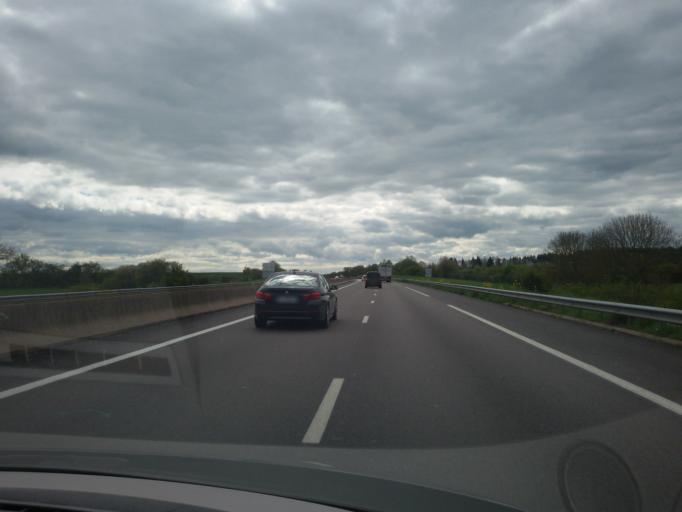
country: FR
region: Bourgogne
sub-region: Departement de la Cote-d'Or
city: Semur-en-Auxois
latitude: 47.3815
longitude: 4.3760
